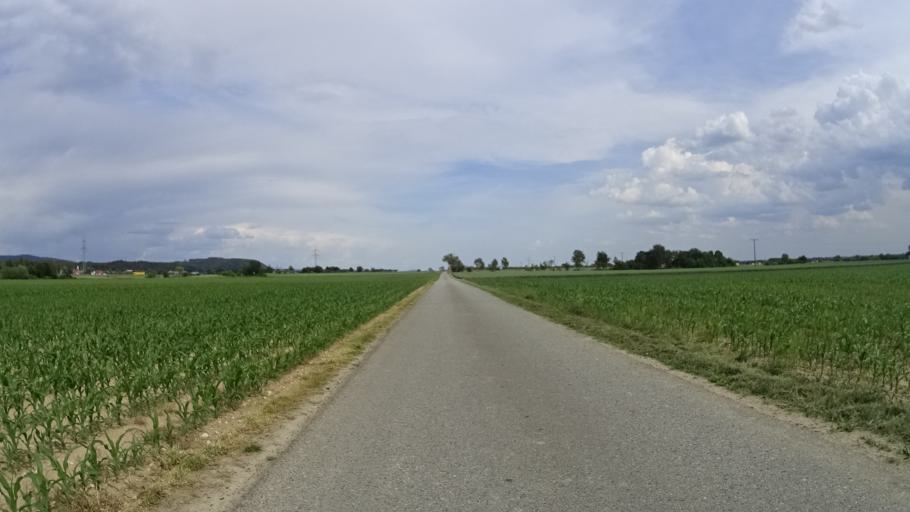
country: DE
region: Bavaria
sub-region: Lower Bavaria
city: Aholfing
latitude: 48.9819
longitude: 12.4557
